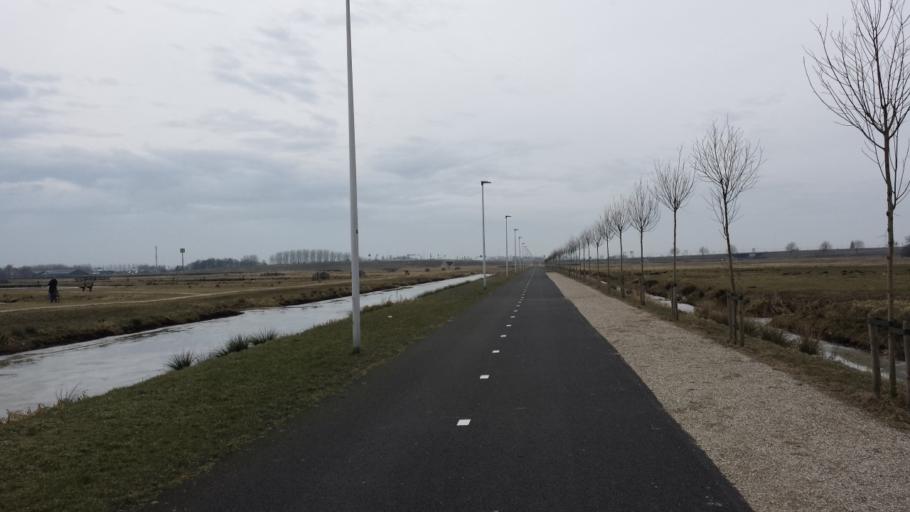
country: NL
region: South Holland
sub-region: Gemeente Gouda
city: Bloemendaal
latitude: 52.0024
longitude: 4.6695
